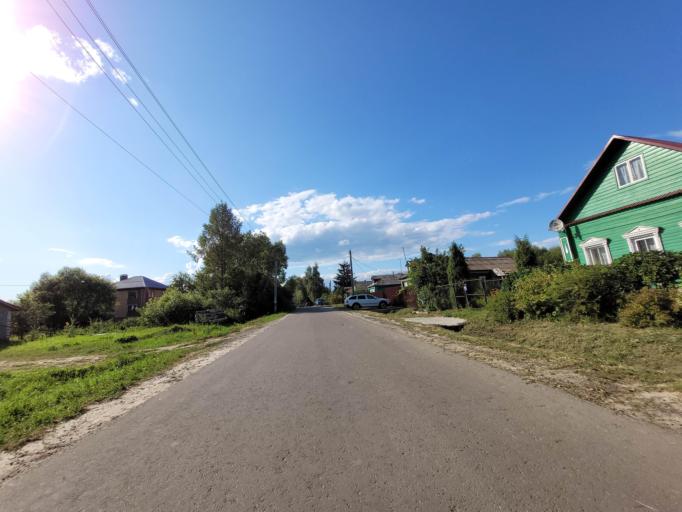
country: RU
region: Moskovskaya
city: Konobeyevo
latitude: 55.4107
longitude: 38.6978
